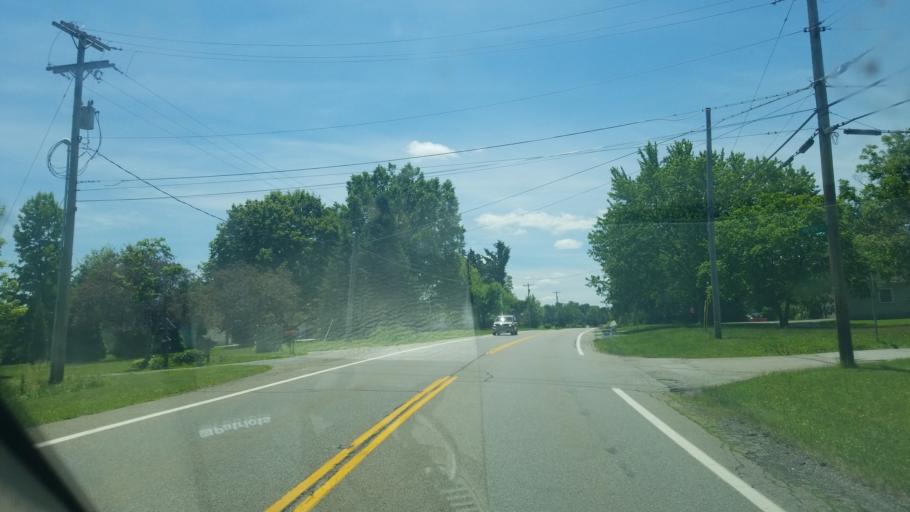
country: US
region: Ohio
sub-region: Columbiana County
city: Columbiana
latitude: 40.9177
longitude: -80.6511
